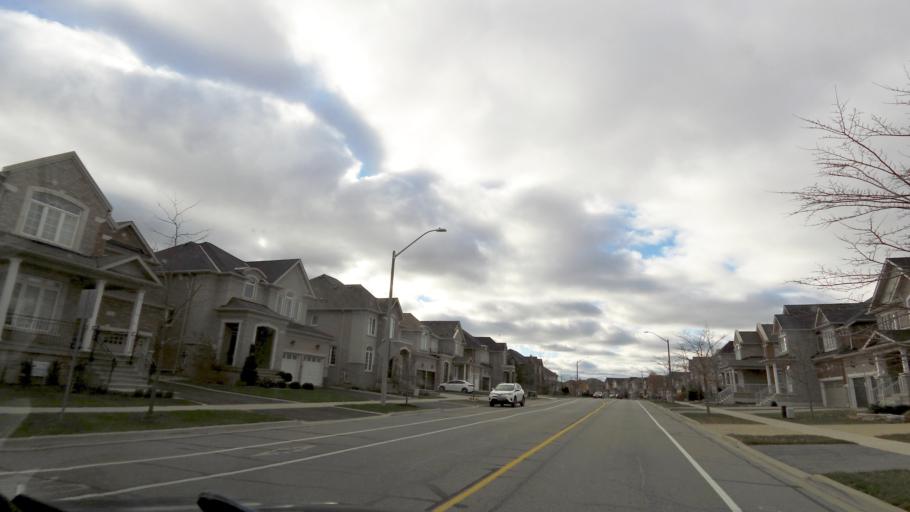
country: CA
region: Ontario
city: Oakville
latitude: 43.4950
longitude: -79.7044
